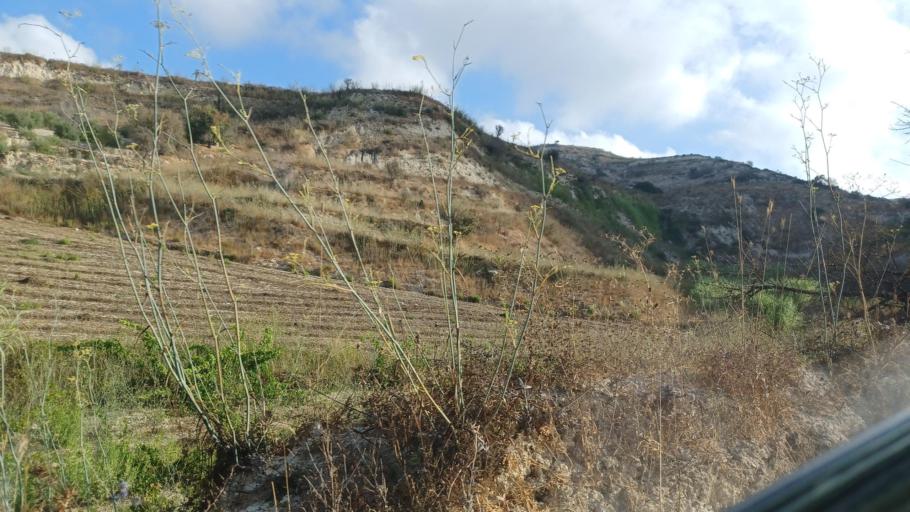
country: CY
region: Pafos
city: Tala
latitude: 34.8805
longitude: 32.4564
